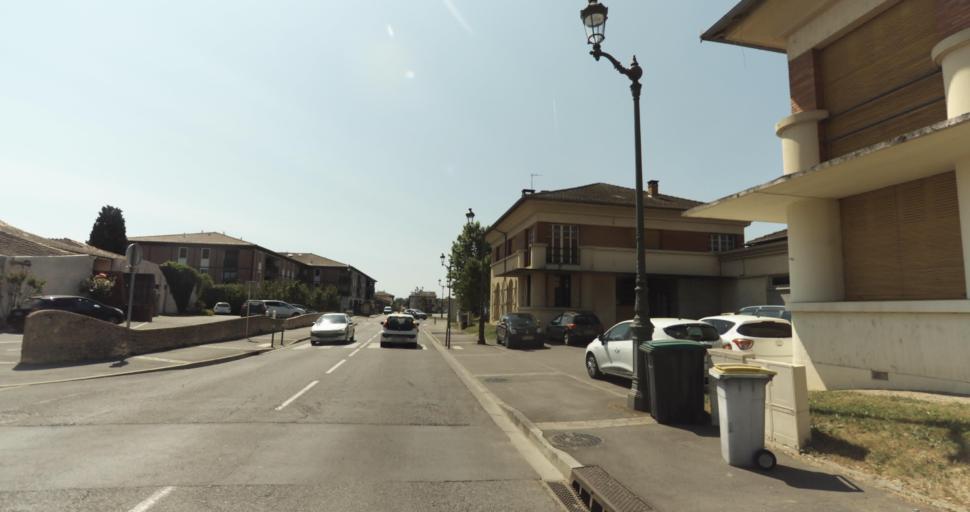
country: FR
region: Midi-Pyrenees
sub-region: Departement de la Haute-Garonne
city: Plaisance-du-Touch
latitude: 43.5679
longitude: 1.2964
